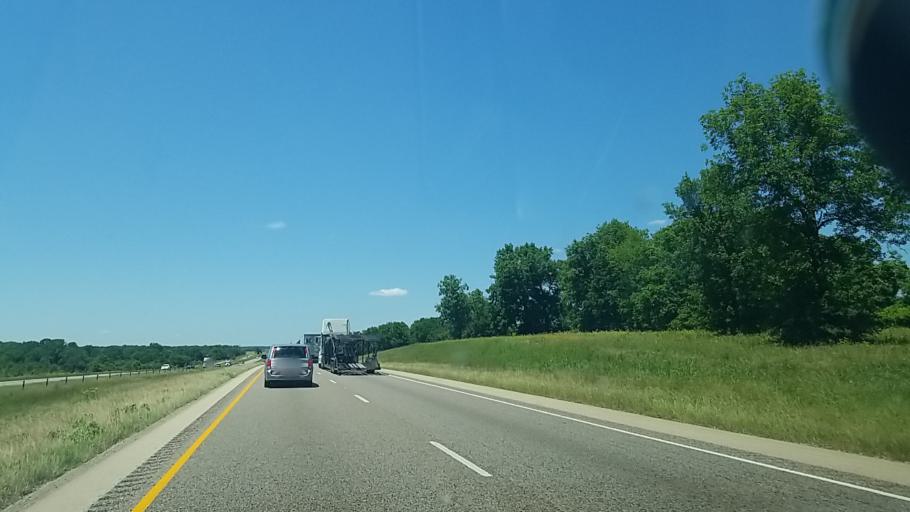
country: US
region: Texas
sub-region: Madison County
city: Madisonville
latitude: 31.0769
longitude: -95.9556
